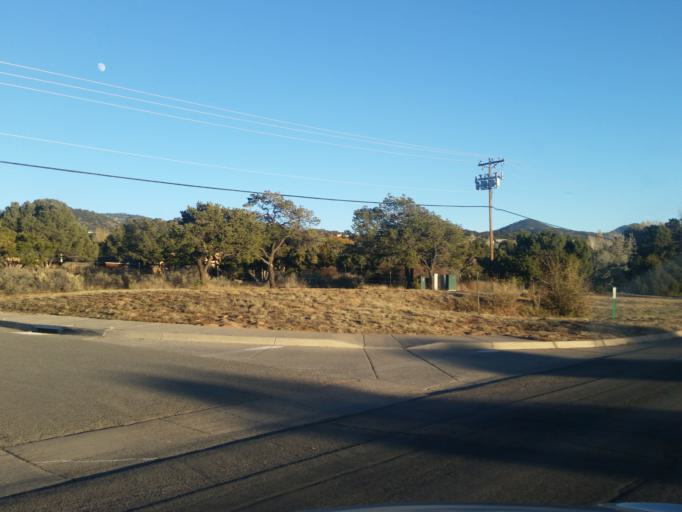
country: US
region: New Mexico
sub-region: Santa Fe County
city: Santa Fe
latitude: 35.6472
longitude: -105.9337
